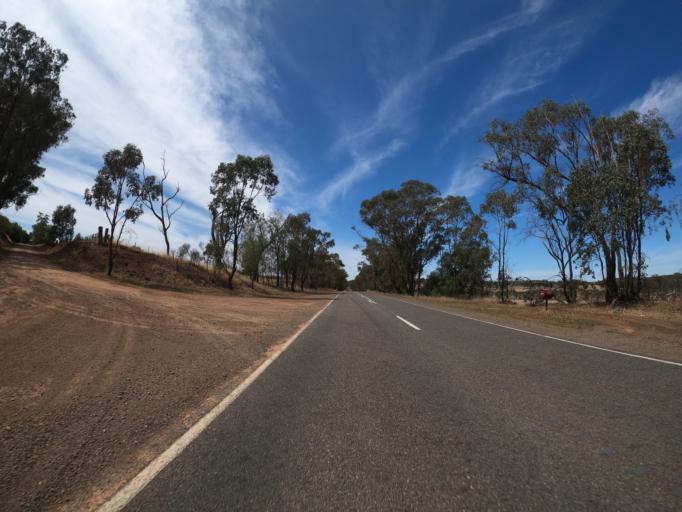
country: AU
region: Victoria
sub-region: Benalla
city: Benalla
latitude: -36.3496
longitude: 145.9623
